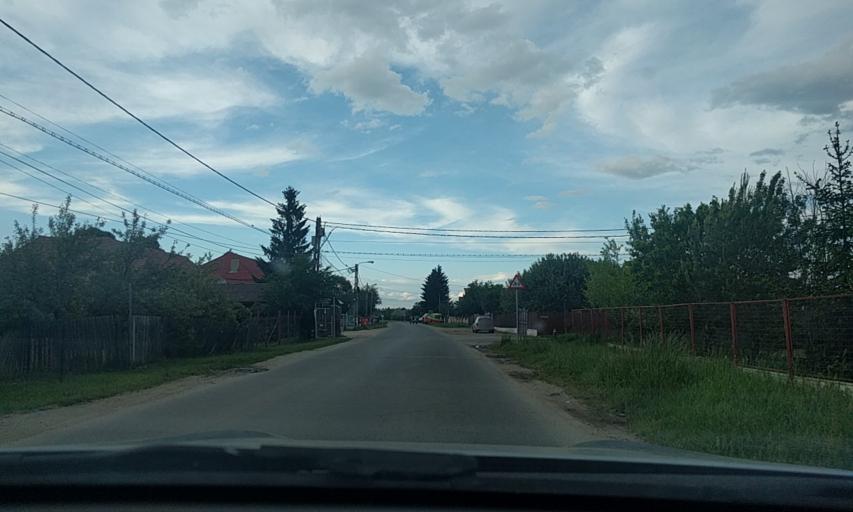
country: RO
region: Brasov
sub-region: Comuna Harman
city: Harman
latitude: 45.7598
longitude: 25.7214
